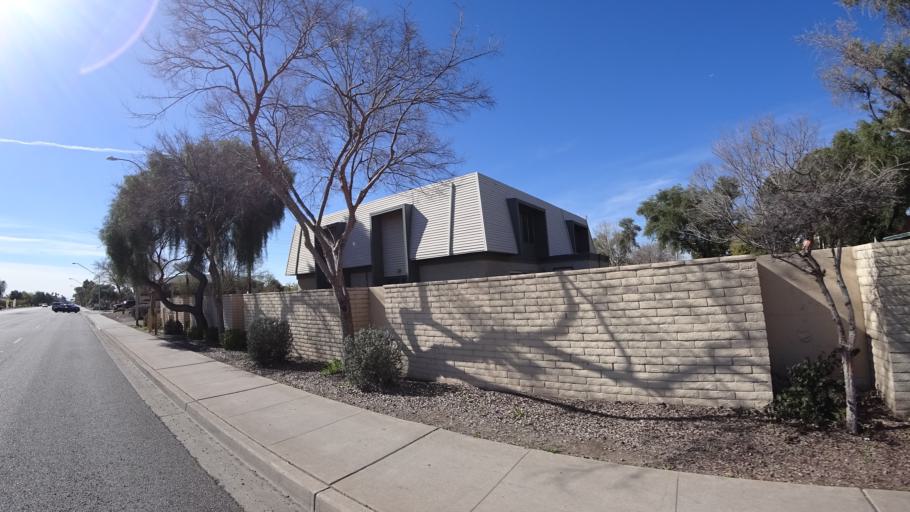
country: US
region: Arizona
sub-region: Maricopa County
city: Glendale
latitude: 33.5647
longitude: -112.1864
